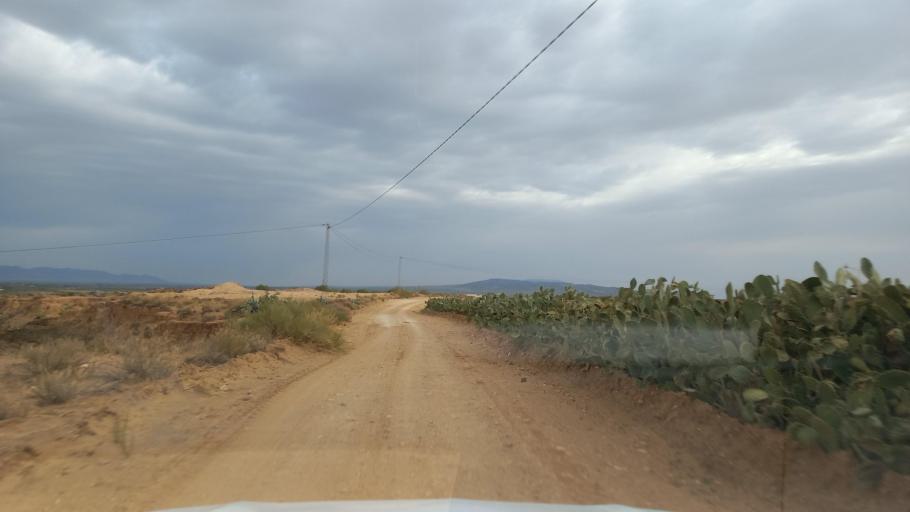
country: TN
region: Al Qasrayn
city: Kasserine
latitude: 35.1882
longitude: 9.0594
